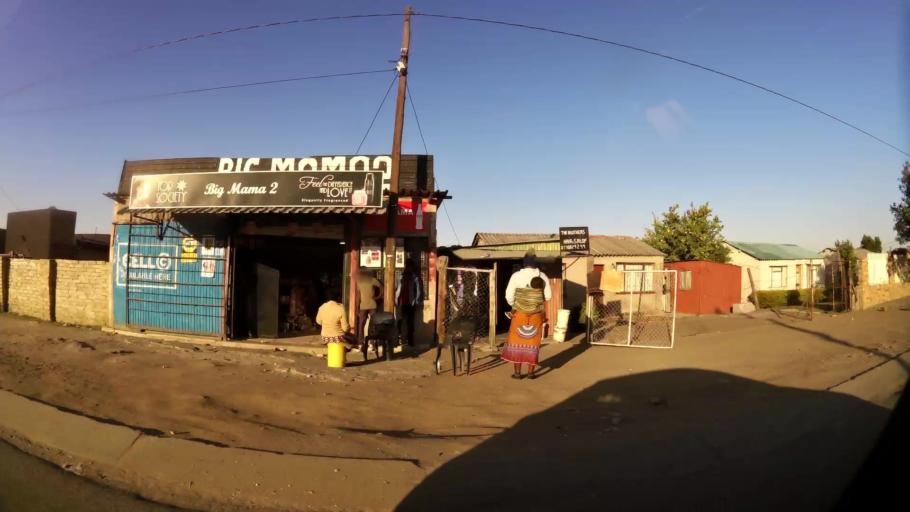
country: ZA
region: North-West
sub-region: Bojanala Platinum District Municipality
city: Rustenburg
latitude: -25.6299
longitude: 27.2155
